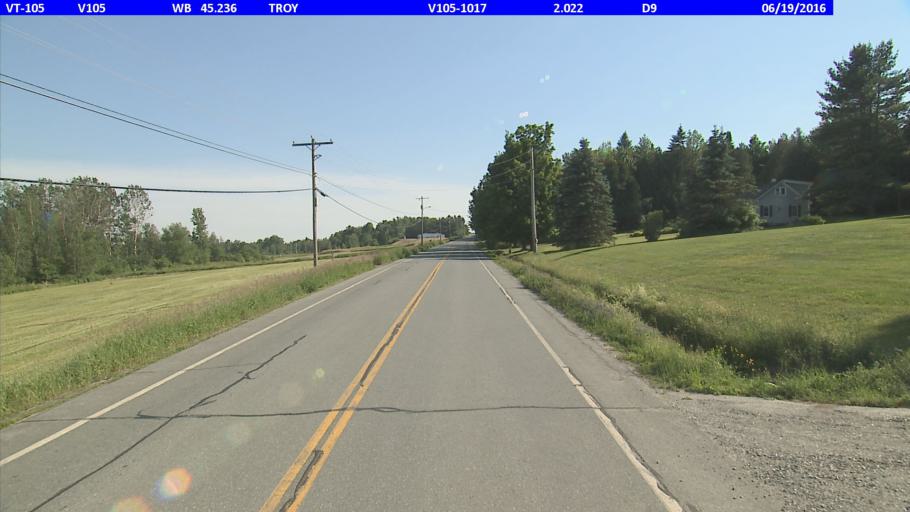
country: US
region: Vermont
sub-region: Orleans County
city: Newport
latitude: 44.9874
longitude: -72.4090
